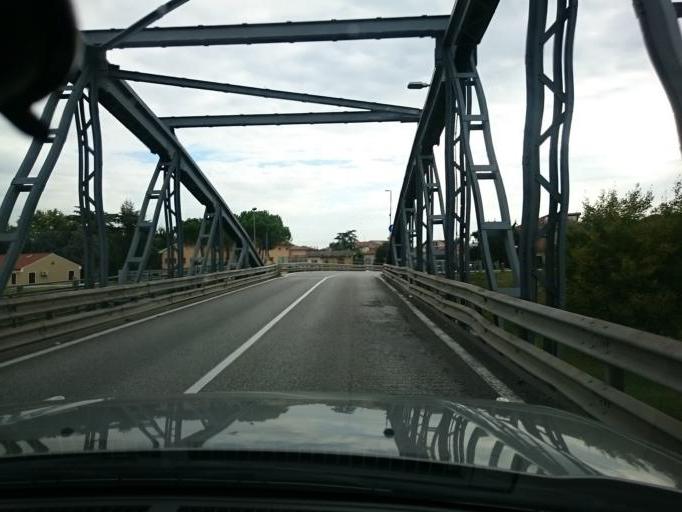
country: IT
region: Veneto
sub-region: Provincia di Padova
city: Ponte San Nicolo
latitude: 45.3644
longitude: 11.9350
